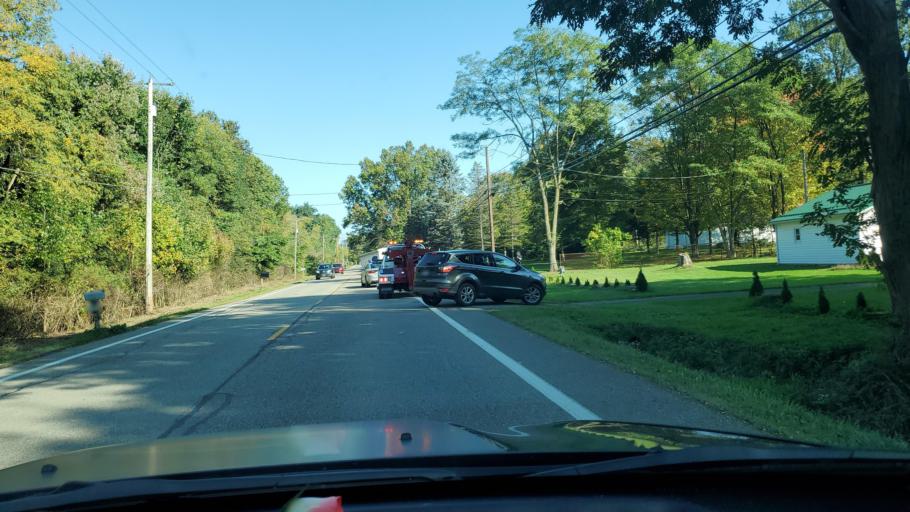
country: US
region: Ohio
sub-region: Trumbull County
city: Brookfield Center
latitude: 41.3253
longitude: -80.5683
